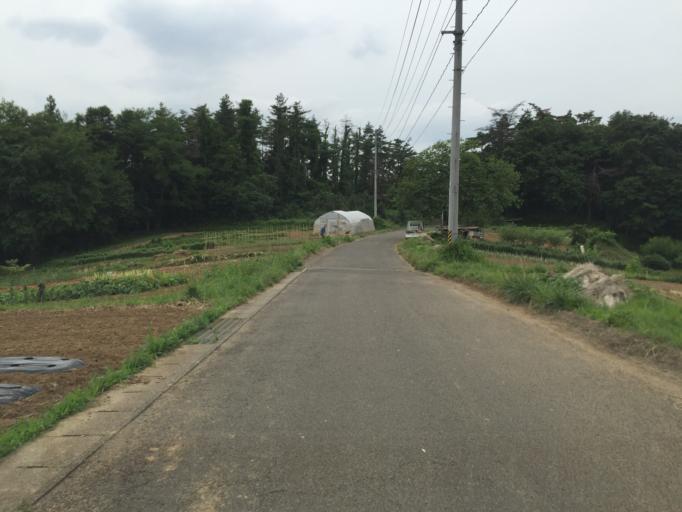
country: JP
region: Fukushima
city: Fukushima-shi
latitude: 37.7134
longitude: 140.4636
